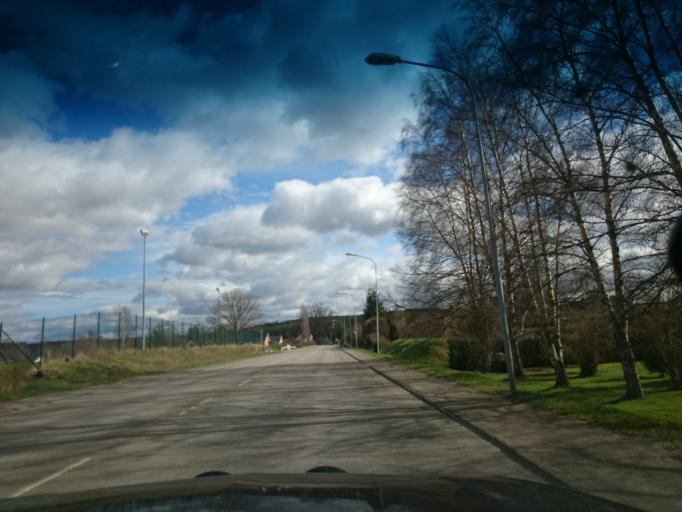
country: SE
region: Joenkoeping
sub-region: Vetlanda Kommun
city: Vetlanda
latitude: 57.4025
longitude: 15.0834
